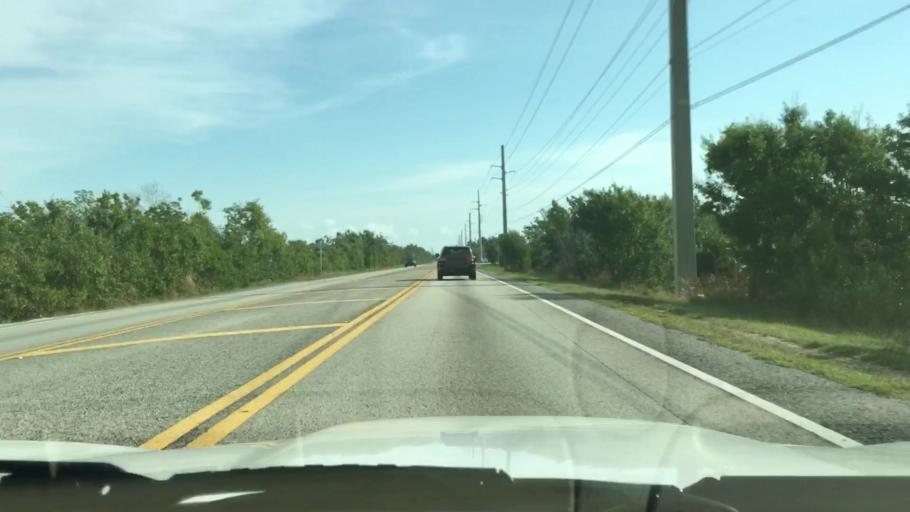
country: US
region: Florida
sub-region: Monroe County
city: Cudjoe Key
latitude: 24.6640
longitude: -81.5083
